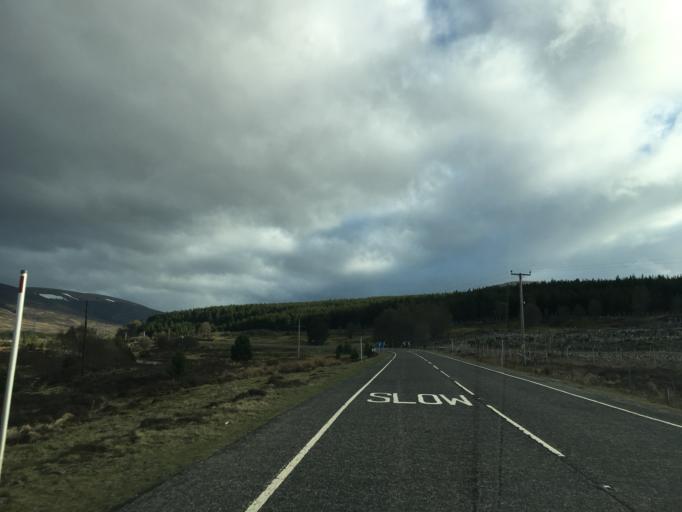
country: GB
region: Scotland
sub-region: Highland
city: Kingussie
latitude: 56.9264
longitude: -4.2400
